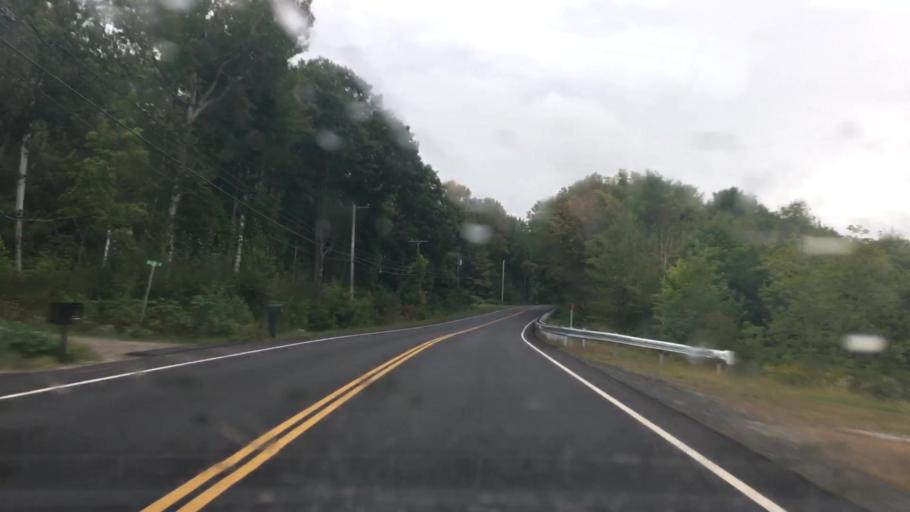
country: US
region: Maine
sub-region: Penobscot County
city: Orrington
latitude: 44.6819
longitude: -68.8090
